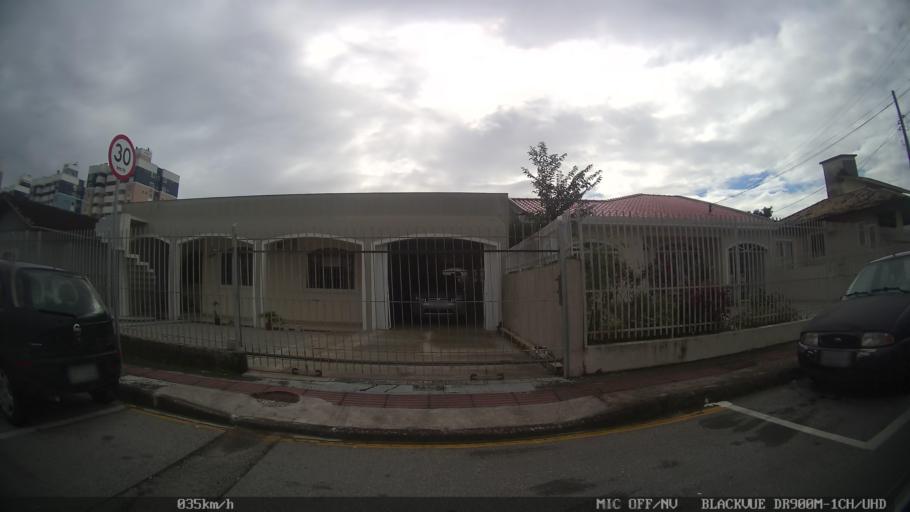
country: BR
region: Santa Catarina
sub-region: Sao Jose
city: Campinas
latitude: -27.5716
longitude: -48.6237
